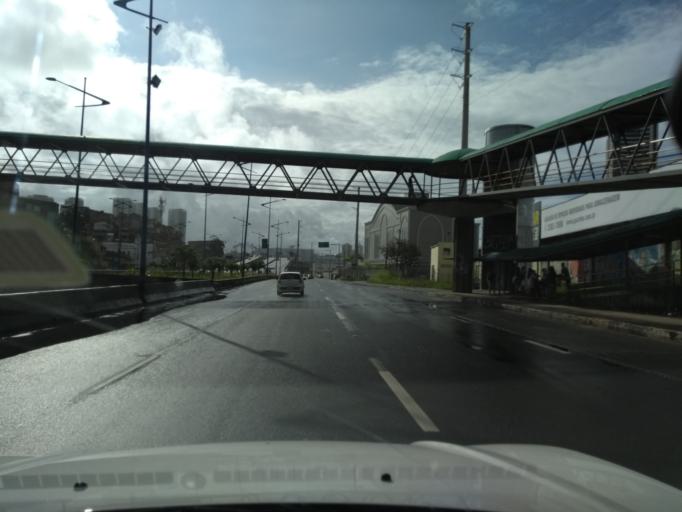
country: BR
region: Bahia
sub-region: Salvador
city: Salvador
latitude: -12.9687
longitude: -38.4848
